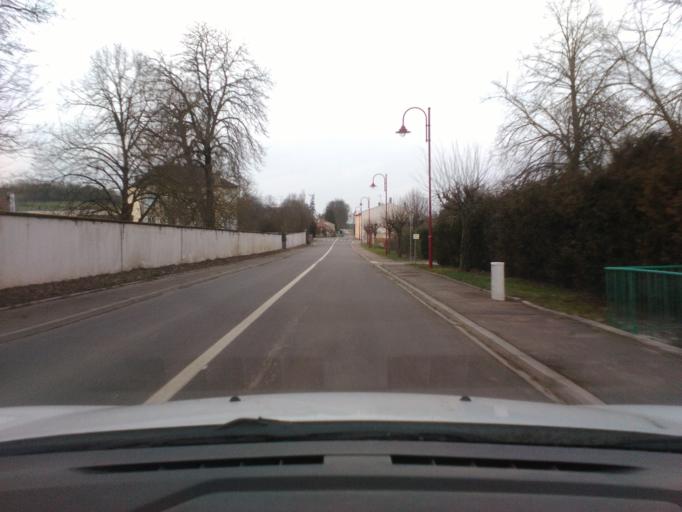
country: FR
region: Lorraine
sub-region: Departement des Vosges
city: Mirecourt
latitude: 48.2459
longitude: 6.1446
